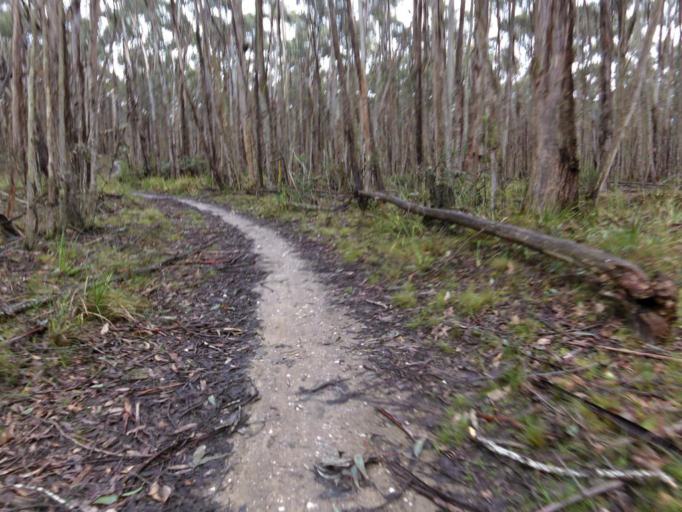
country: AU
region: Victoria
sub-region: Moorabool
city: Bacchus Marsh
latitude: -37.4076
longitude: 144.4874
